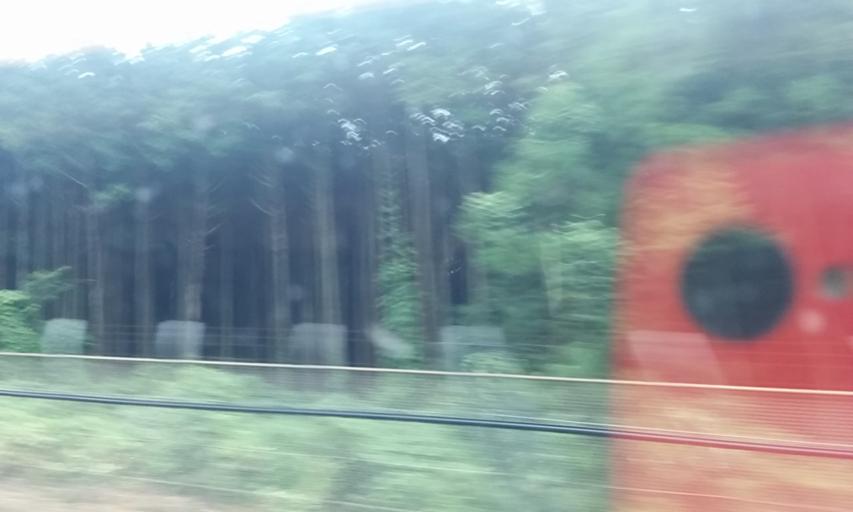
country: JP
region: Tochigi
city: Kuroiso
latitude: 37.0068
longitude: 140.0899
